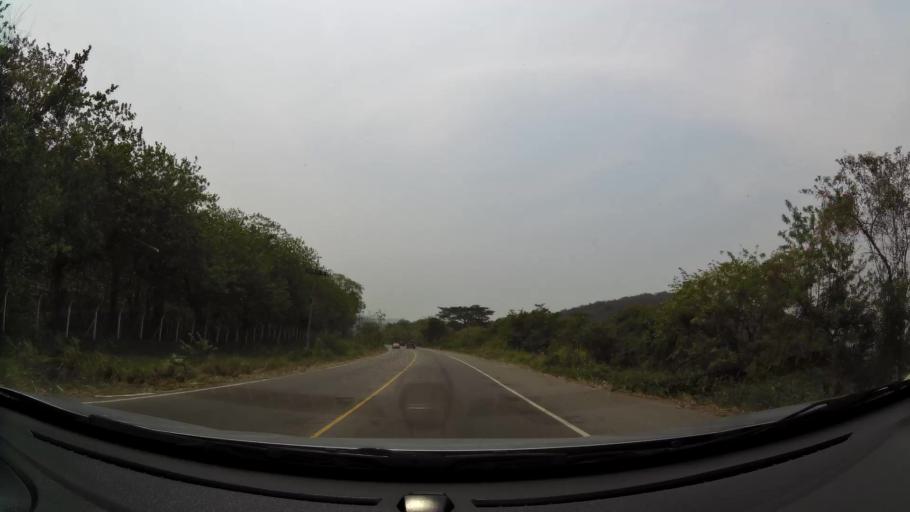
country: HN
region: Cortes
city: Bejuco
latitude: 15.1687
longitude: -87.9510
